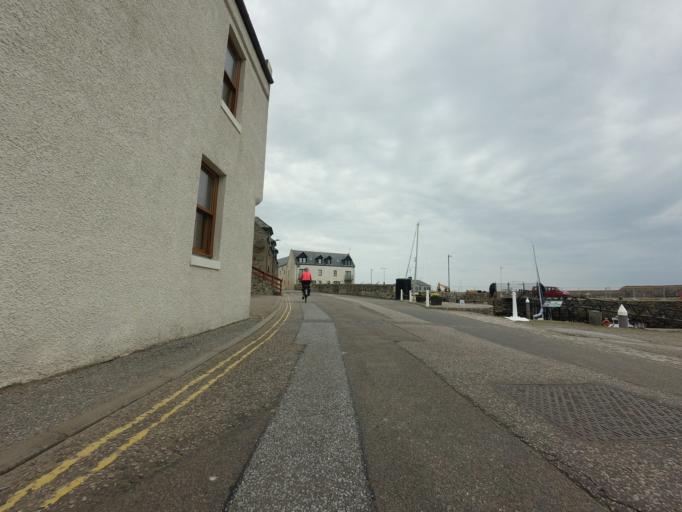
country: GB
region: Scotland
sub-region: Aberdeenshire
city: Banff
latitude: 57.6699
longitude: -2.5235
